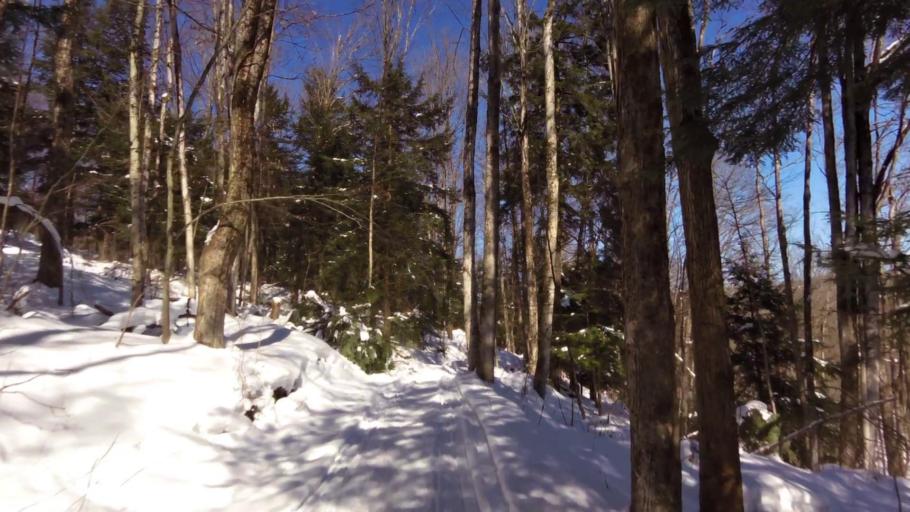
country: US
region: New York
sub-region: Allegany County
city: Cuba
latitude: 42.2811
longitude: -78.2313
